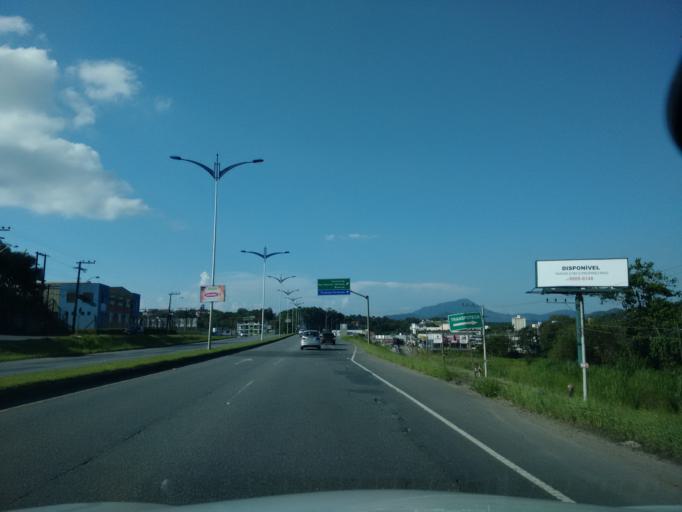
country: BR
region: Santa Catarina
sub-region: Blumenau
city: Blumenau
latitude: -26.8849
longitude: -49.0696
